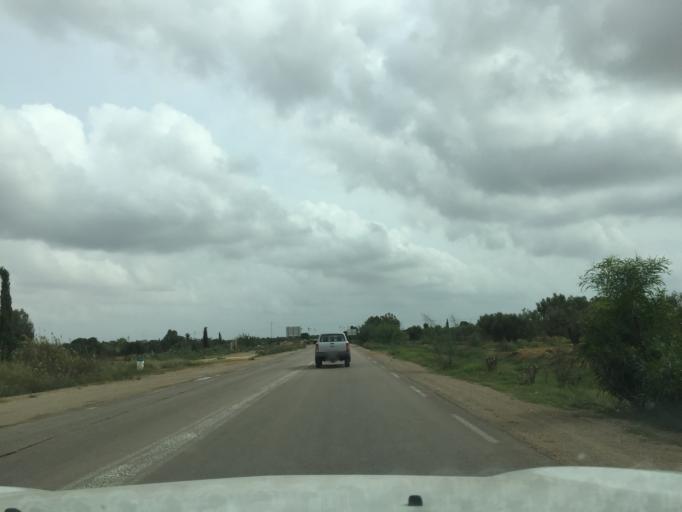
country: TN
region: Al Munastir
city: Bani Hassan
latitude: 35.5427
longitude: 10.8598
